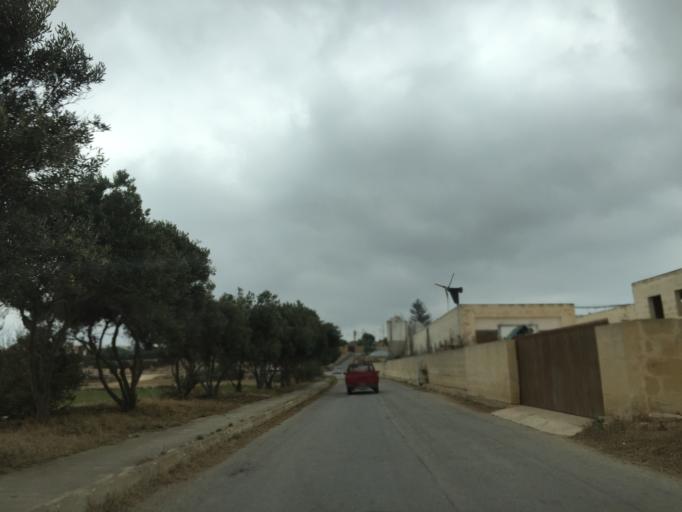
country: MT
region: L-Imgarr
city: Imgarr
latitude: 35.9156
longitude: 14.3724
